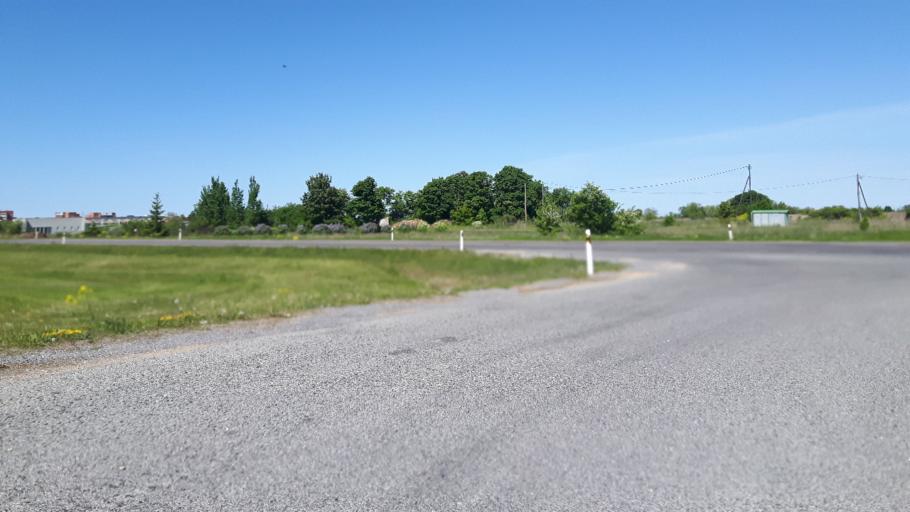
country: EE
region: Ida-Virumaa
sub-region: Sillamaee linn
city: Sillamae
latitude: 59.3872
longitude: 27.8083
